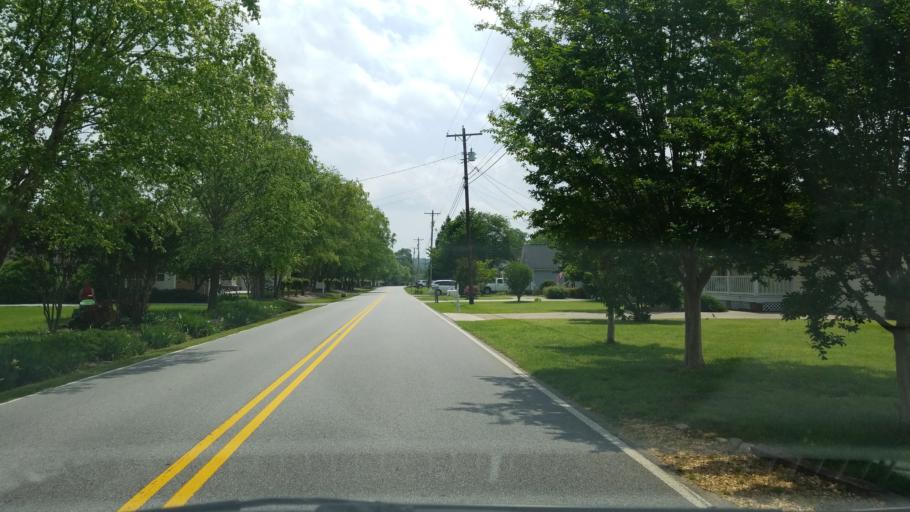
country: US
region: Tennessee
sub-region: Hamilton County
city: Soddy-Daisy
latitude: 35.2259
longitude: -85.2231
